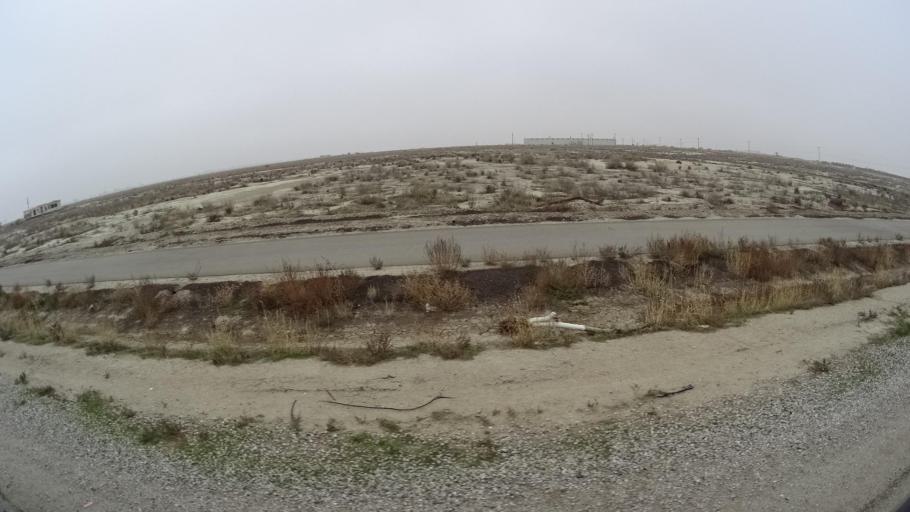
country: US
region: California
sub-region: Kern County
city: Rosedale
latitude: 35.2459
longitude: -119.2527
